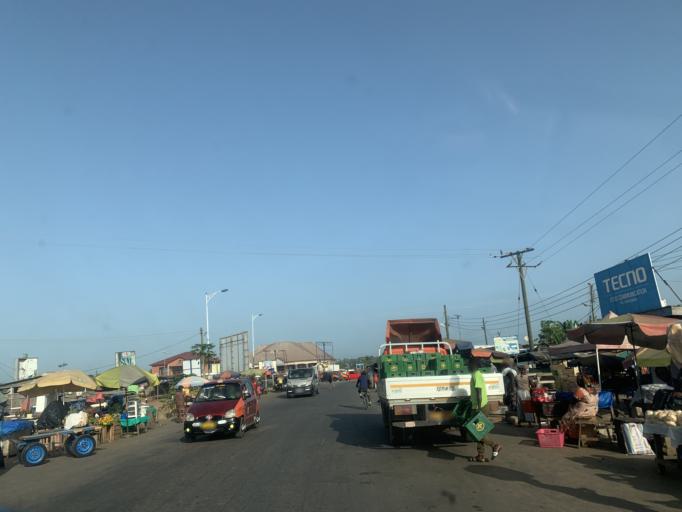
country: GH
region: Central
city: Saltpond
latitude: 5.2676
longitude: -1.0175
